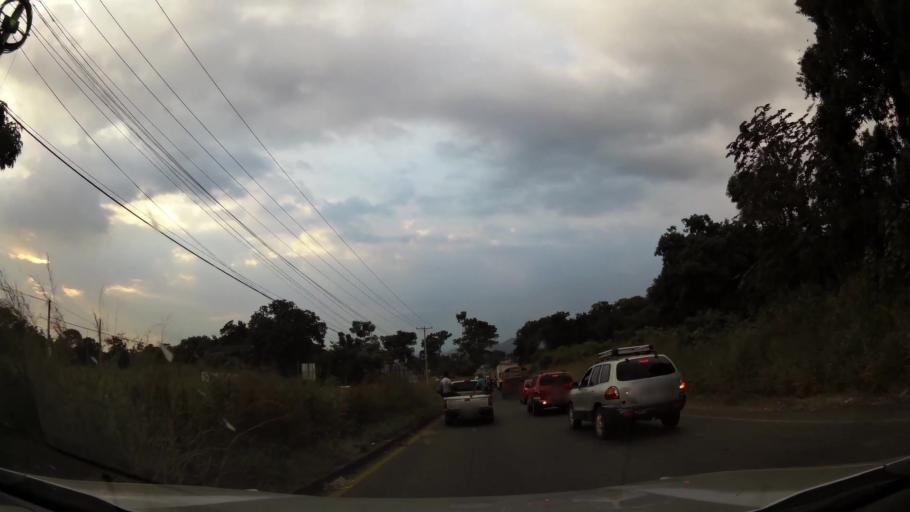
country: GT
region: Escuintla
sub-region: Municipio de Escuintla
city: Escuintla
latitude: 14.2843
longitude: -90.7904
